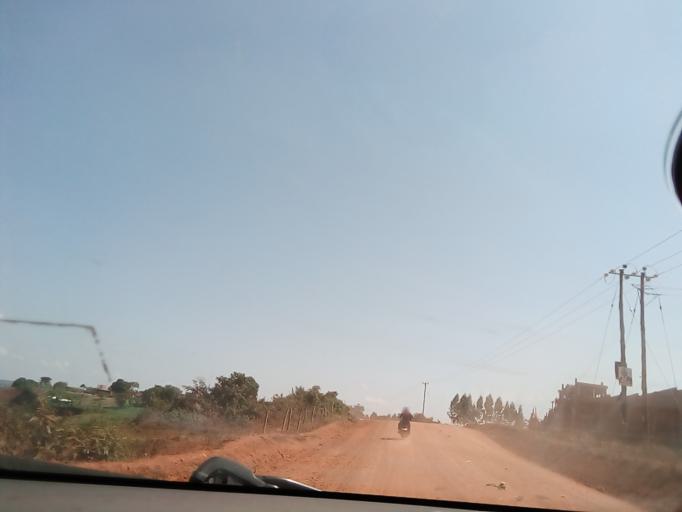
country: UG
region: Central Region
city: Masaka
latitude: -0.3627
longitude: 31.7480
